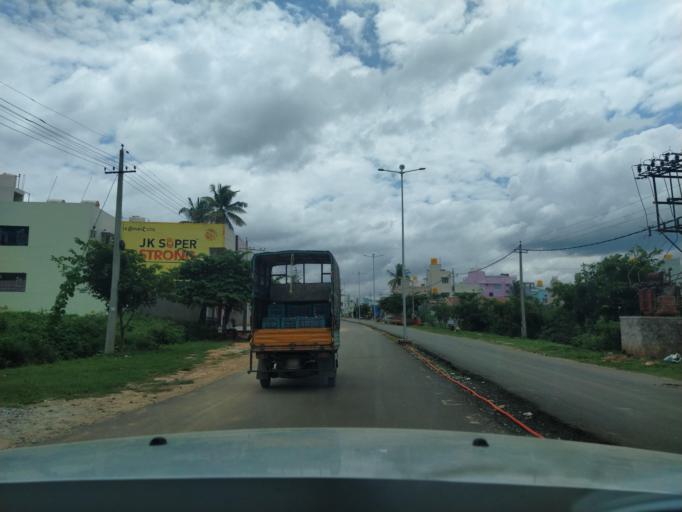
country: IN
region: Karnataka
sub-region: Tumkur
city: Tumkur
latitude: 13.3135
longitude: 77.1358
